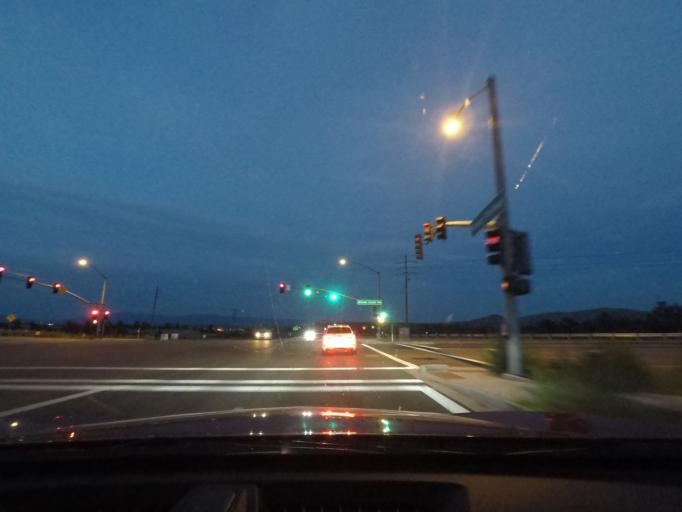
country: US
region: Arizona
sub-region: Yavapai County
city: Prescott
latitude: 34.6291
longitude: -112.4395
